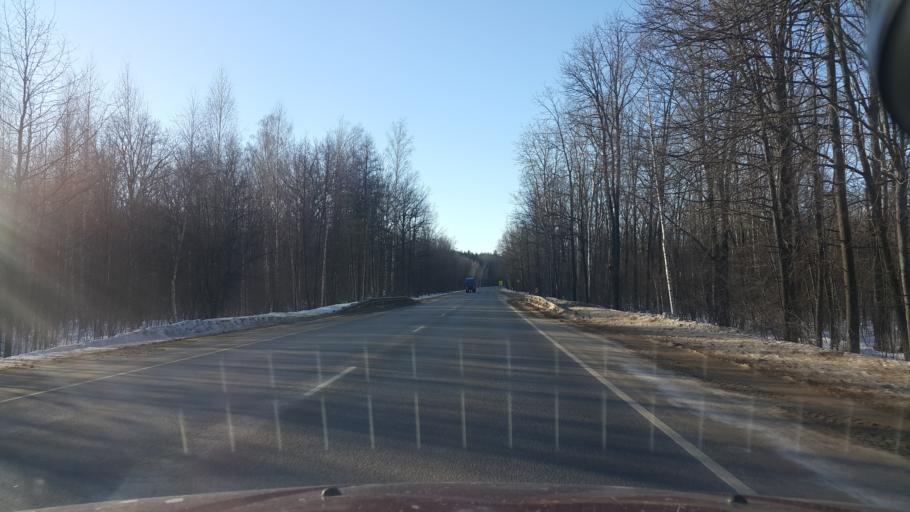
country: RU
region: Tambov
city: Novaya Lyada
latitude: 52.6954
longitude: 41.5473
